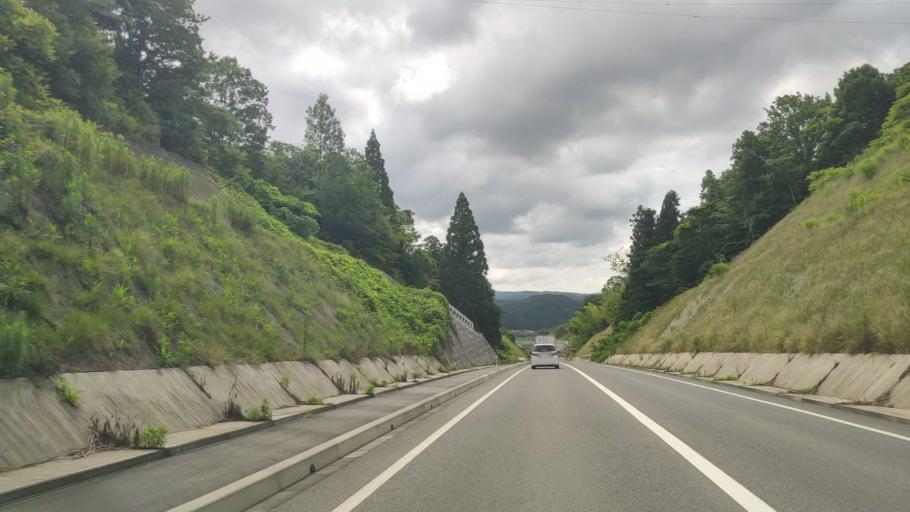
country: JP
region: Tottori
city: Yonago
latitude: 35.3755
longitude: 133.4078
